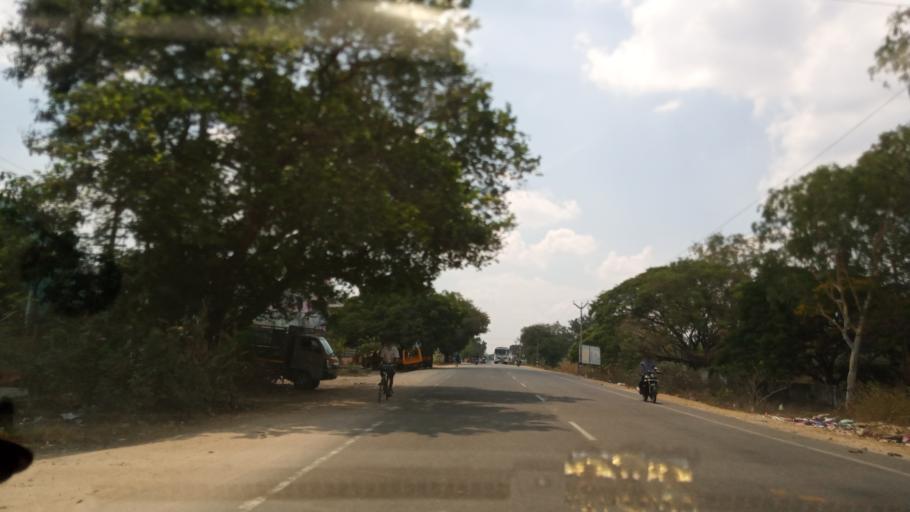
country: IN
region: Tamil Nadu
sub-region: Vellore
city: Walajapet
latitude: 12.9211
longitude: 79.3788
